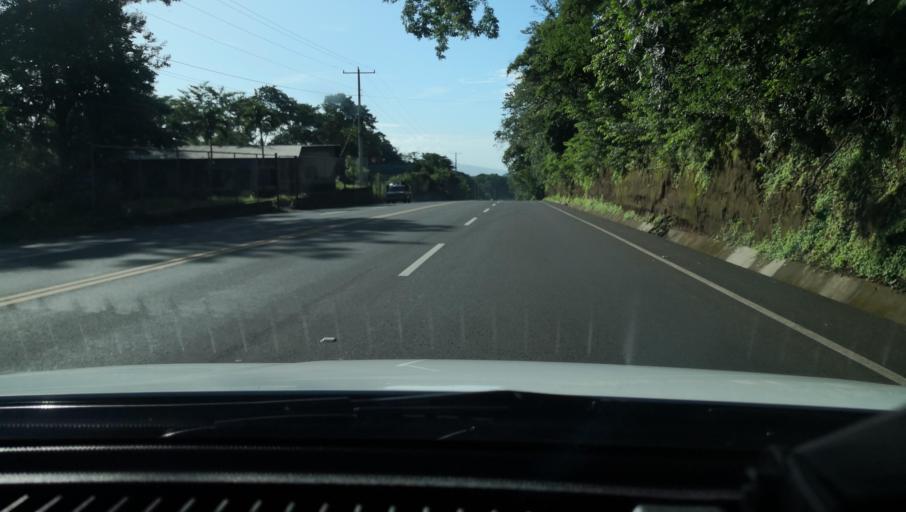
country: NI
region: Granada
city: Nandaime
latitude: 11.7896
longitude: -86.0643
